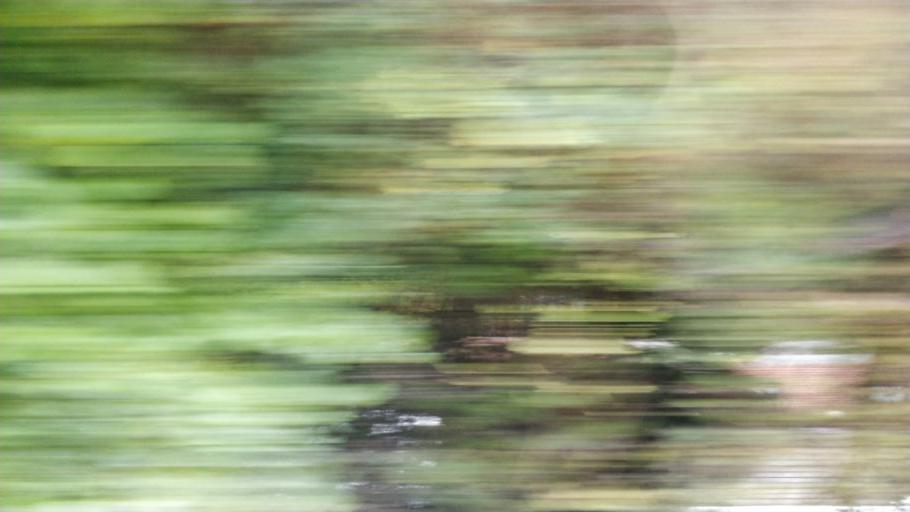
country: GB
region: England
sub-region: Borough of Wigan
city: Atherton
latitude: 53.5296
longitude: -2.4804
